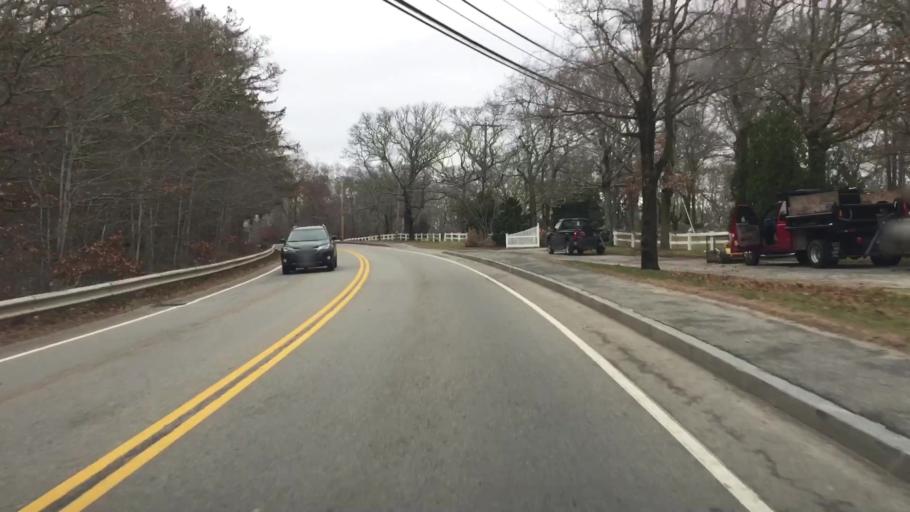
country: US
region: Massachusetts
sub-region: Barnstable County
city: Teaticket
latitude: 41.5676
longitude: -70.6074
